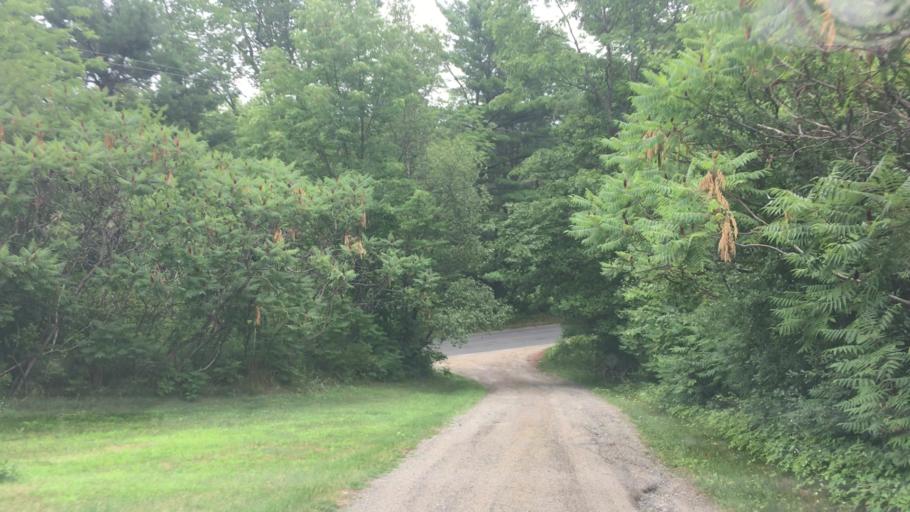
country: US
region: New York
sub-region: Essex County
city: Keeseville
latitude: 44.4359
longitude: -73.6202
